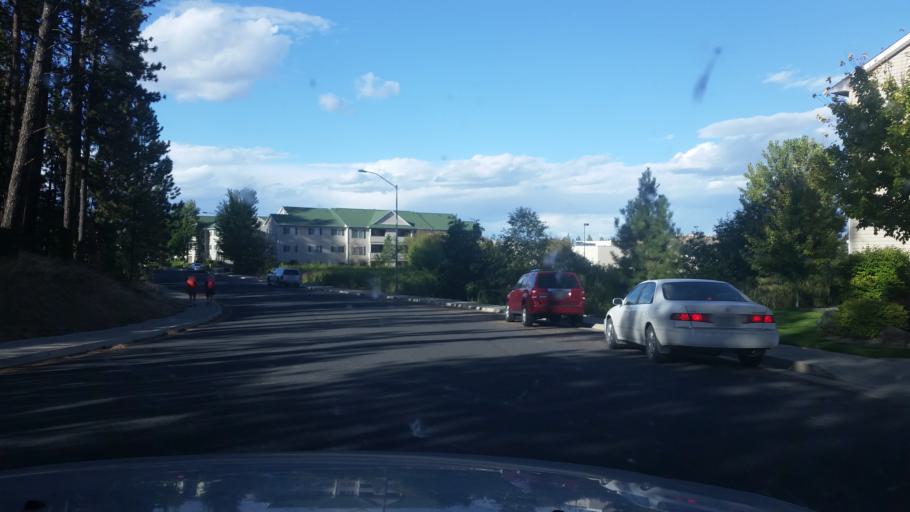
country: US
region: Washington
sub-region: Spokane County
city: Cheney
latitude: 47.5045
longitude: -117.5692
